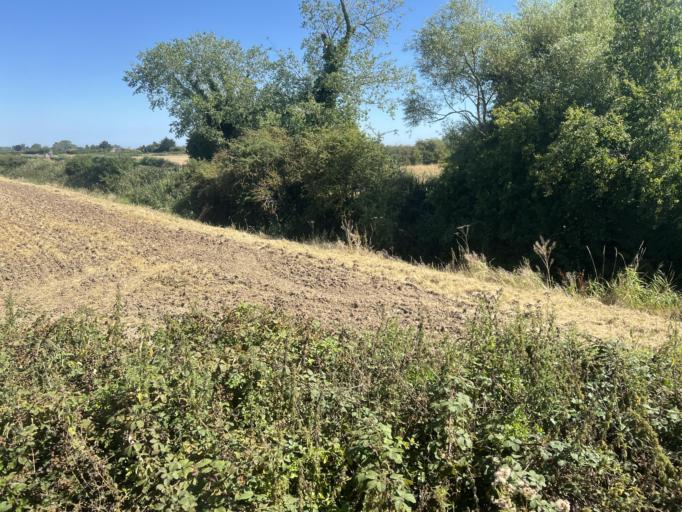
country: GB
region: England
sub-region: Lincolnshire
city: Wainfleet All Saints
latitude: 53.1237
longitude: 0.1988
